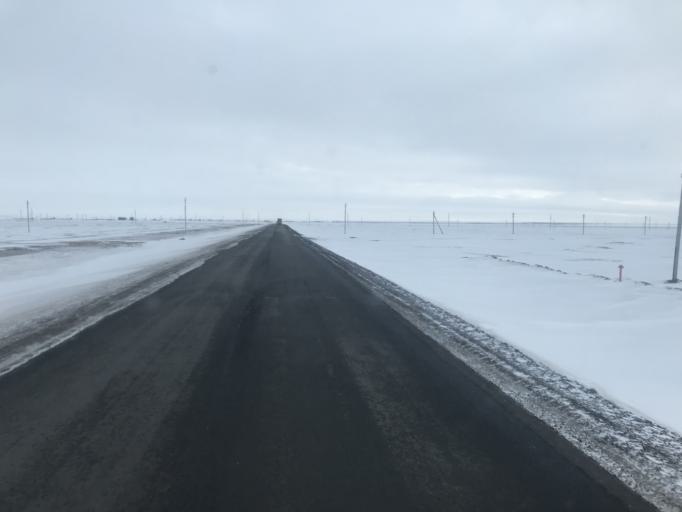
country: RU
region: Orenburg
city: Dombarovskiy
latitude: 49.9538
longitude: 60.0892
